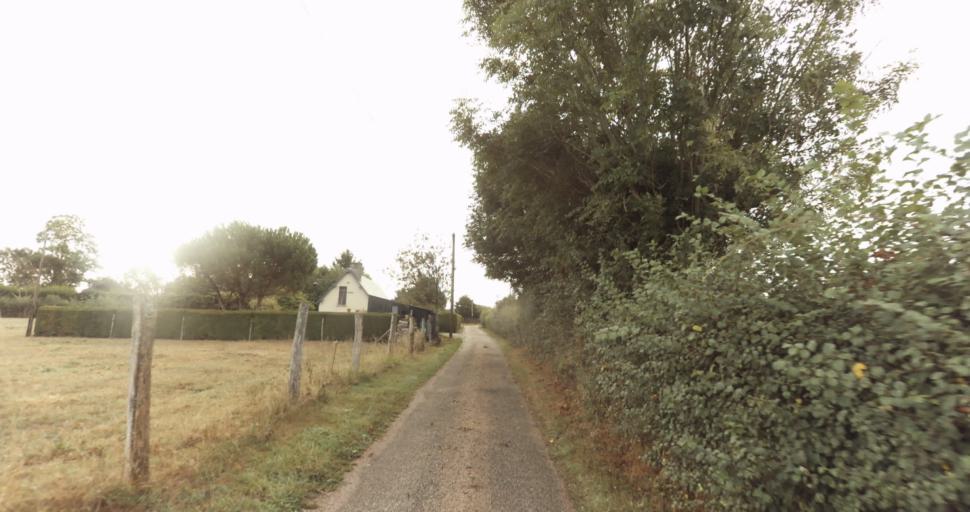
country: FR
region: Lower Normandy
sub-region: Departement de l'Orne
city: Vimoutiers
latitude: 48.9218
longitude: 0.2207
